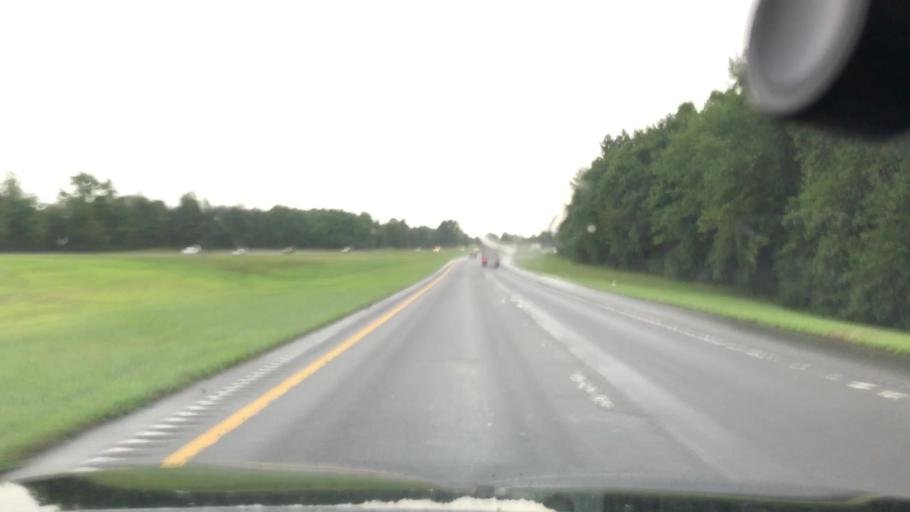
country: US
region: North Carolina
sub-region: Iredell County
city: Statesville
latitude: 35.9298
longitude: -80.8553
